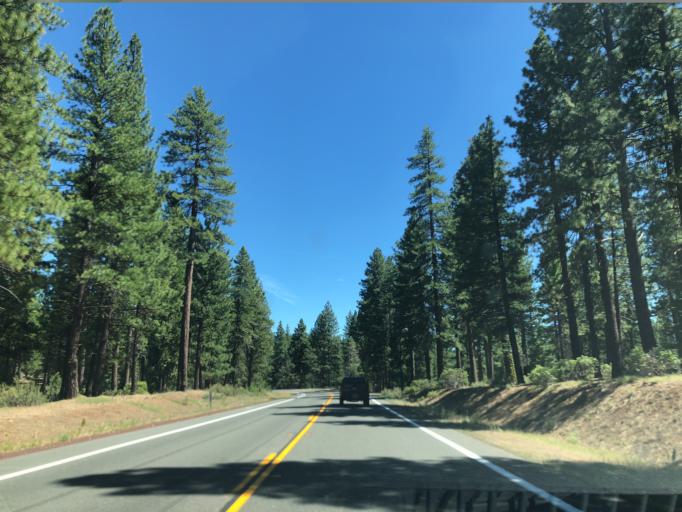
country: US
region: California
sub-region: Lassen County
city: Susanville
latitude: 40.4199
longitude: -120.7854
